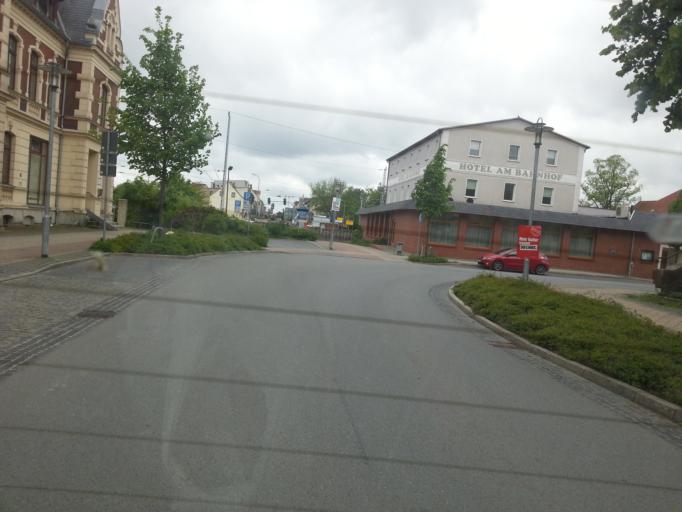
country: DE
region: Mecklenburg-Vorpommern
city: Waren
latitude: 53.5196
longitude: 12.6832
